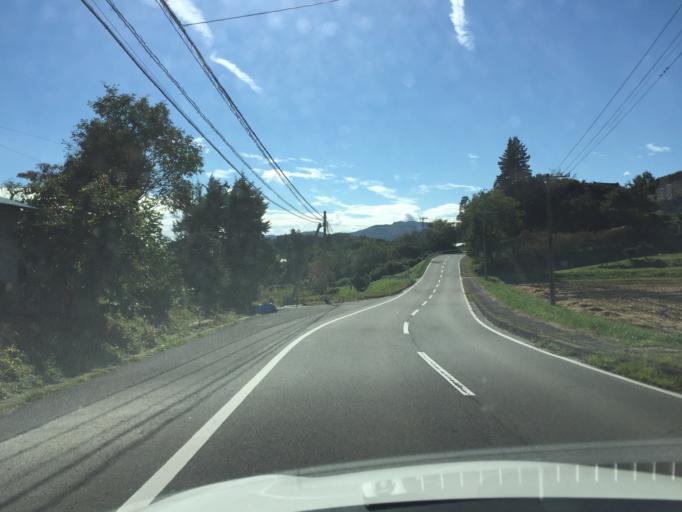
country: JP
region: Fukushima
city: Funehikimachi-funehiki
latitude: 37.4214
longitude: 140.5498
